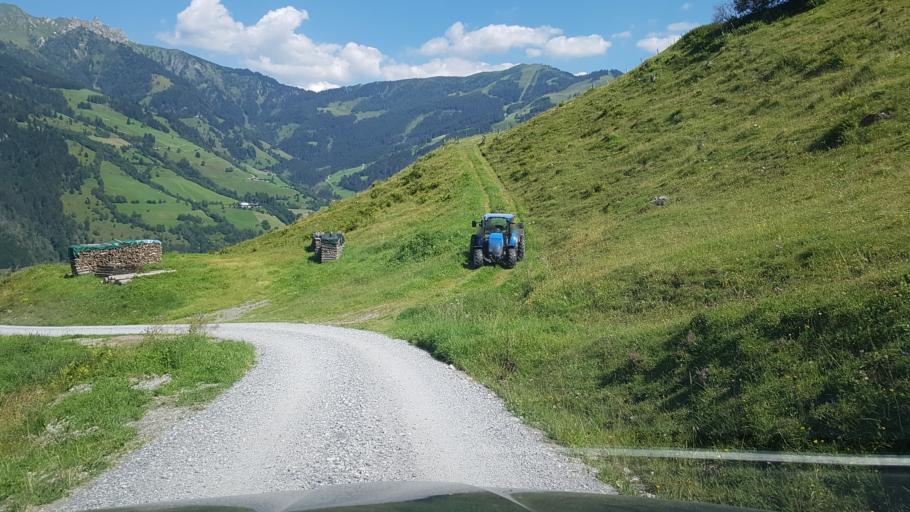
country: AT
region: Salzburg
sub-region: Politischer Bezirk Sankt Johann im Pongau
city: Dorfgastein
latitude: 47.2511
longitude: 13.0794
